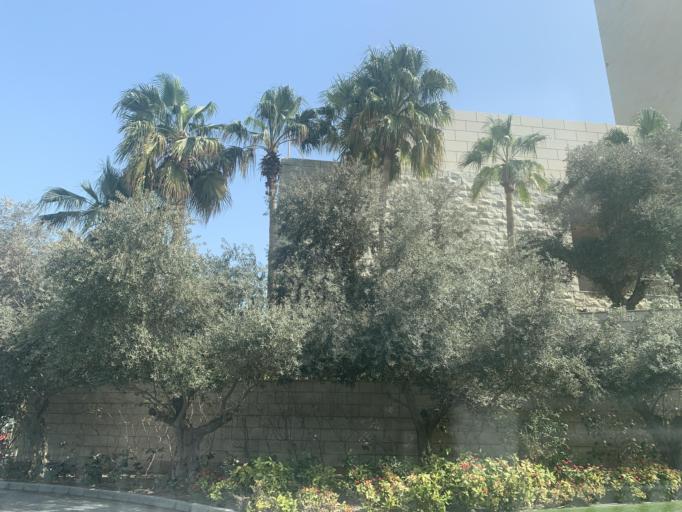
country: BH
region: Muharraq
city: Al Muharraq
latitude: 26.2486
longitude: 50.5818
